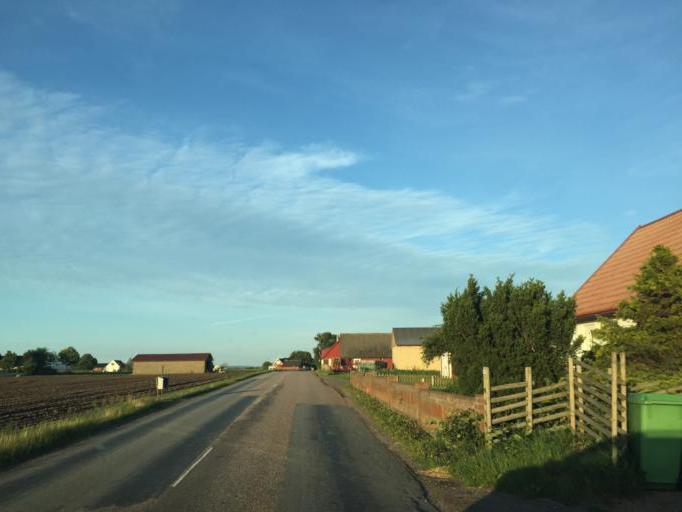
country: SE
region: Skane
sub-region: Angelholms Kommun
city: Vejbystrand
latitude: 56.3161
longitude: 12.7872
